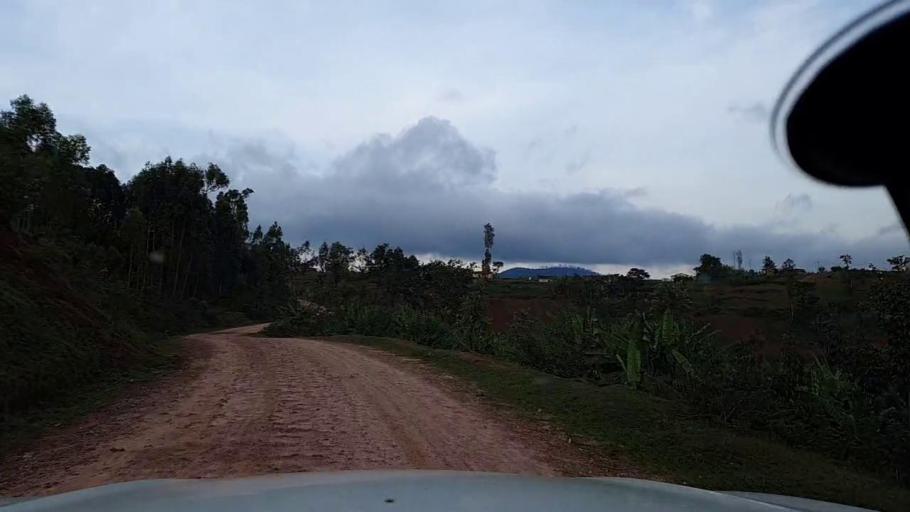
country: RW
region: Southern Province
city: Gitarama
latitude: -2.2095
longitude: 29.6028
